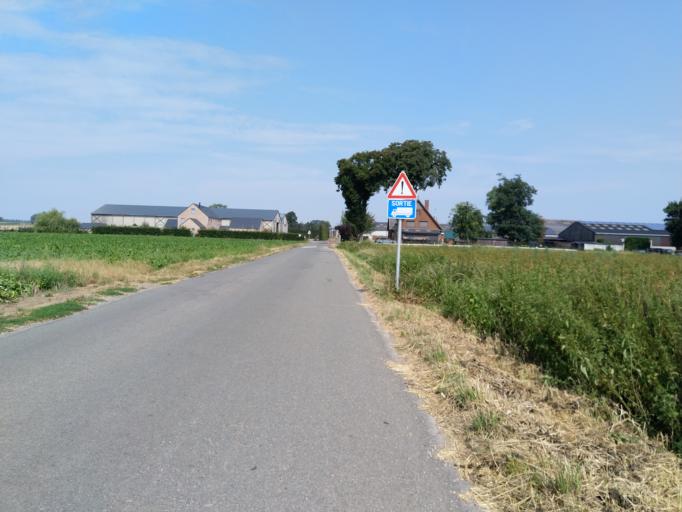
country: BE
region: Wallonia
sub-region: Province du Hainaut
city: Roeulx
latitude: 50.4866
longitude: 4.0575
